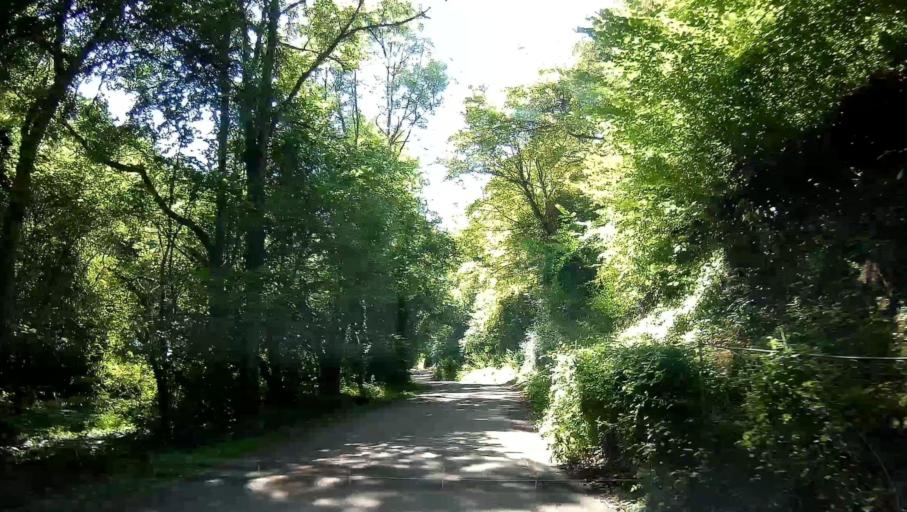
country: FR
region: Bourgogne
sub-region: Departement de la Cote-d'Or
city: Nolay
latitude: 46.9799
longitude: 4.6555
